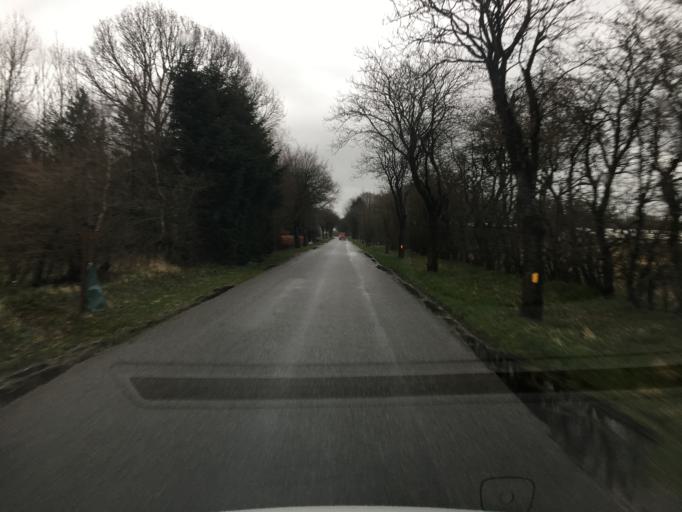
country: DK
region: South Denmark
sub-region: Aabenraa Kommune
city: Tinglev
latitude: 54.9048
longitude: 9.2774
